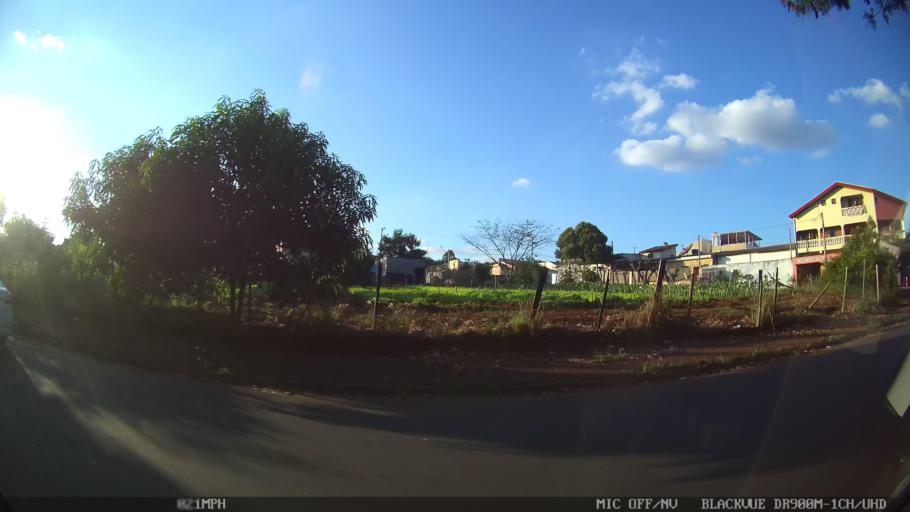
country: BR
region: Sao Paulo
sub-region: Santa Barbara D'Oeste
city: Santa Barbara d'Oeste
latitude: -22.7493
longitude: -47.3792
